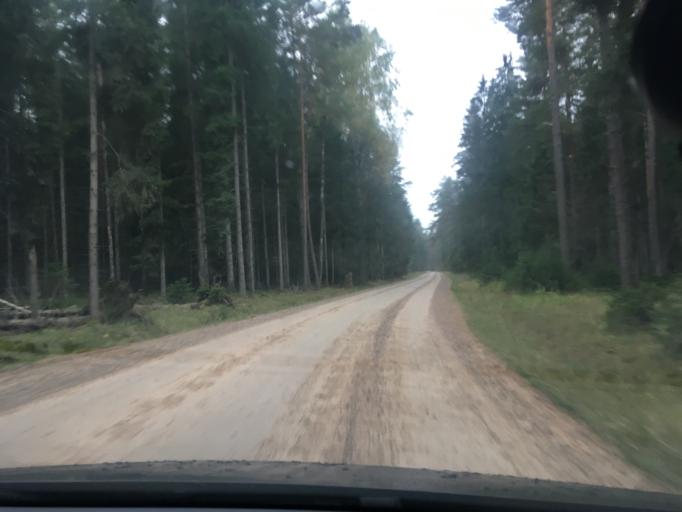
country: LV
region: Kuldigas Rajons
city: Kuldiga
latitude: 56.9959
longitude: 21.9786
